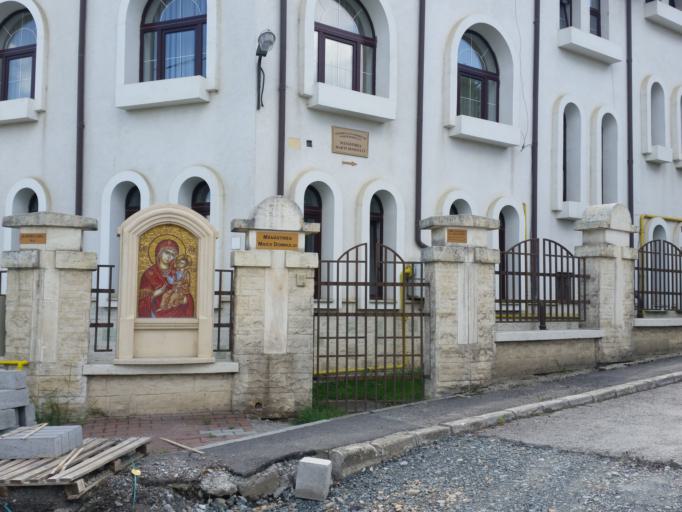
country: RO
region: Cluj
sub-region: Municipiul Cluj-Napoca
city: Cluj-Napoca
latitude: 46.7556
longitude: 23.6204
